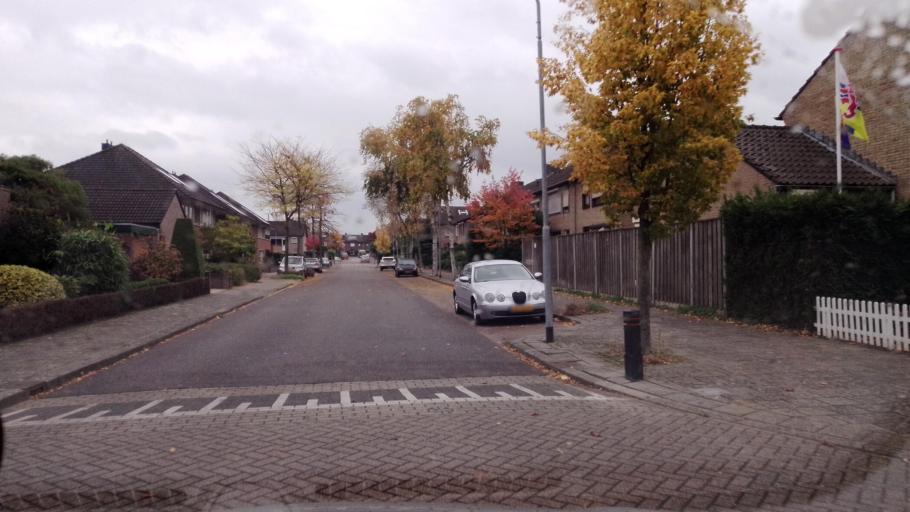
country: NL
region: Limburg
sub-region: Gemeente Venlo
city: Venlo
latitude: 51.3743
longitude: 6.1441
